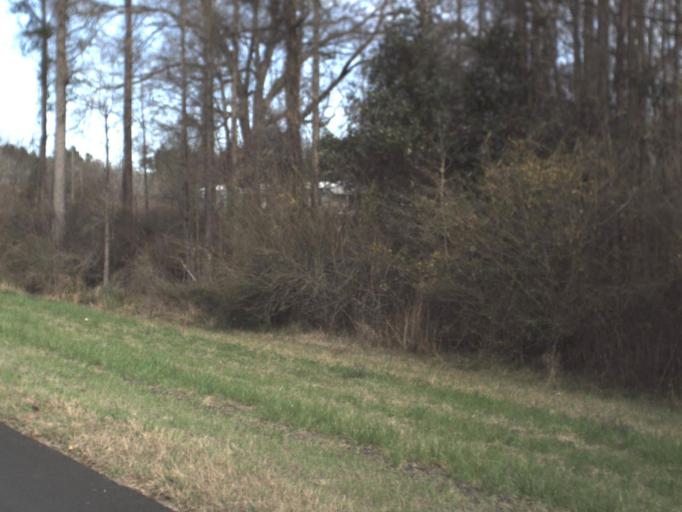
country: US
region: Florida
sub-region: Washington County
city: Chipley
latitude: 30.6761
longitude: -85.3939
